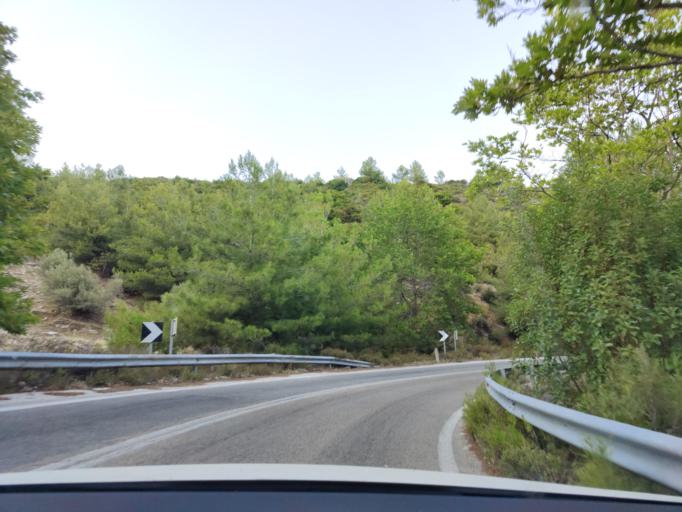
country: GR
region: East Macedonia and Thrace
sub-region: Nomos Kavalas
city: Potamia
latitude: 40.6217
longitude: 24.7589
